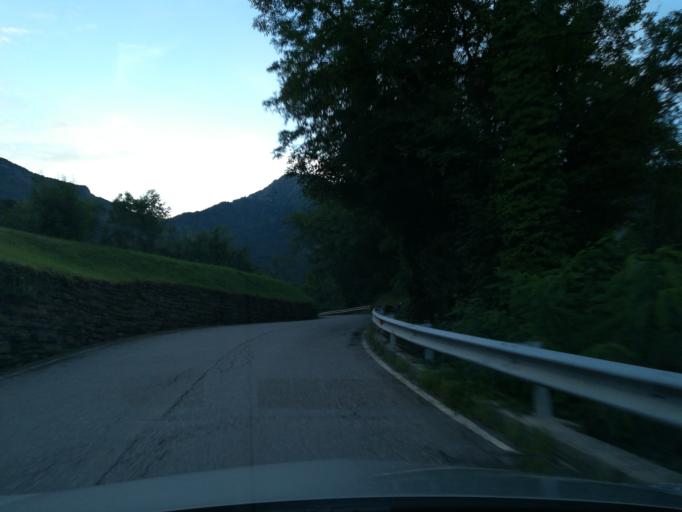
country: IT
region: Lombardy
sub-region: Provincia di Bergamo
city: Rota d'Imagna
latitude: 45.8251
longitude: 9.5068
